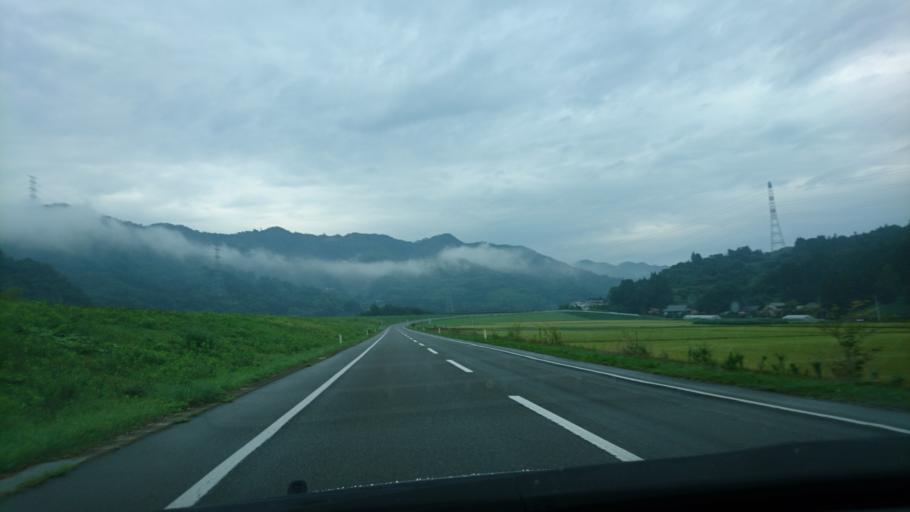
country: JP
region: Iwate
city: Ichinoseki
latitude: 38.9308
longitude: 141.2539
